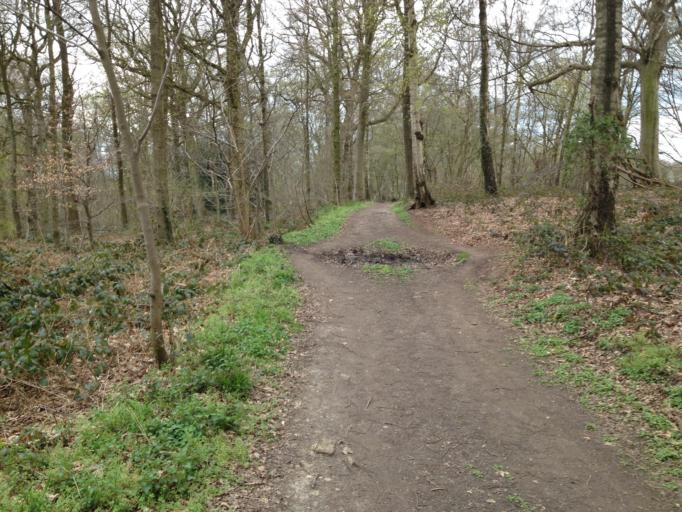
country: BE
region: Wallonia
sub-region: Province de Liege
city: Aubel
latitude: 50.7629
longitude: 5.8845
